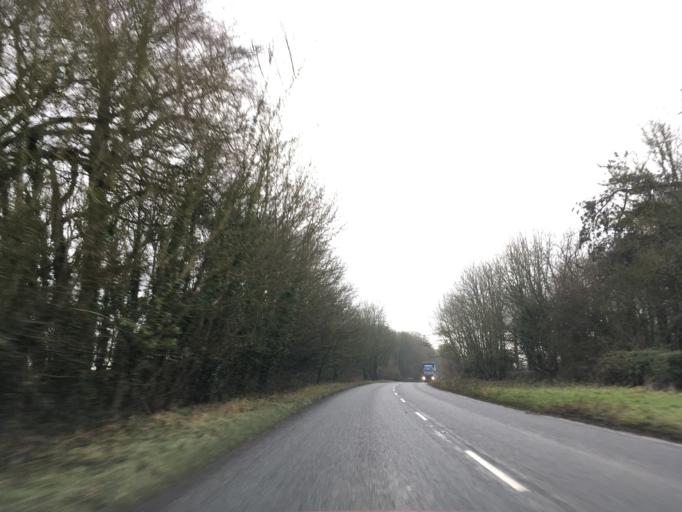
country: GB
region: England
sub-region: Gloucestershire
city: Nailsworth
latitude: 51.6312
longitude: -2.2547
